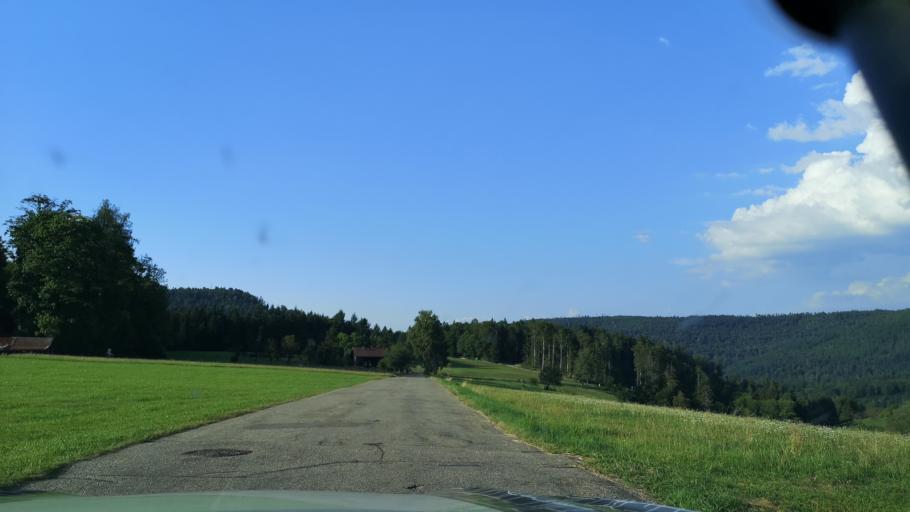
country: DE
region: Baden-Wuerttemberg
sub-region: Karlsruhe Region
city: Bad Herrenalb
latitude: 48.7689
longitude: 8.4405
